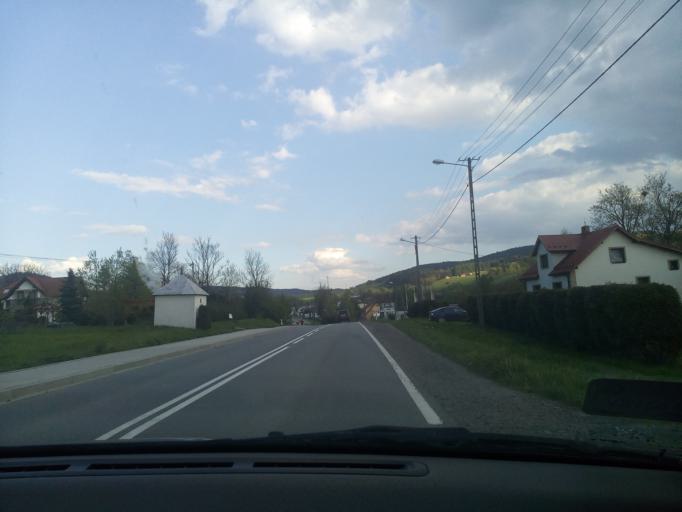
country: PL
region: Lesser Poland Voivodeship
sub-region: Powiat nowosadecki
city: Labowa
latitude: 49.5305
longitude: 20.8510
